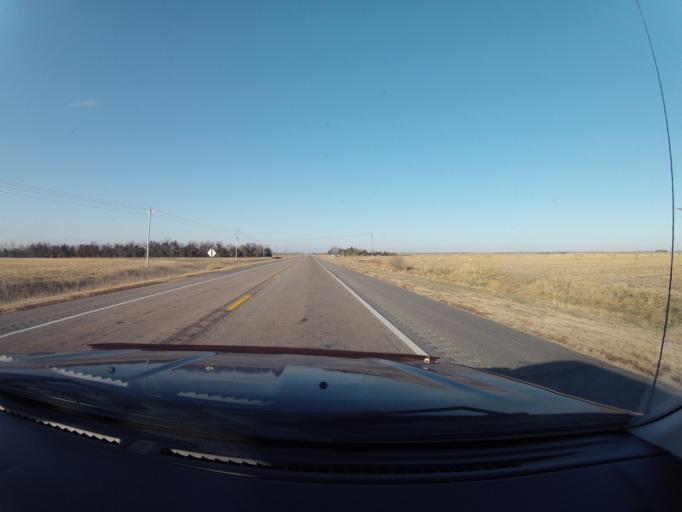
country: US
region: Nebraska
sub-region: Kearney County
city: Minden
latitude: 40.6299
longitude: -98.9514
